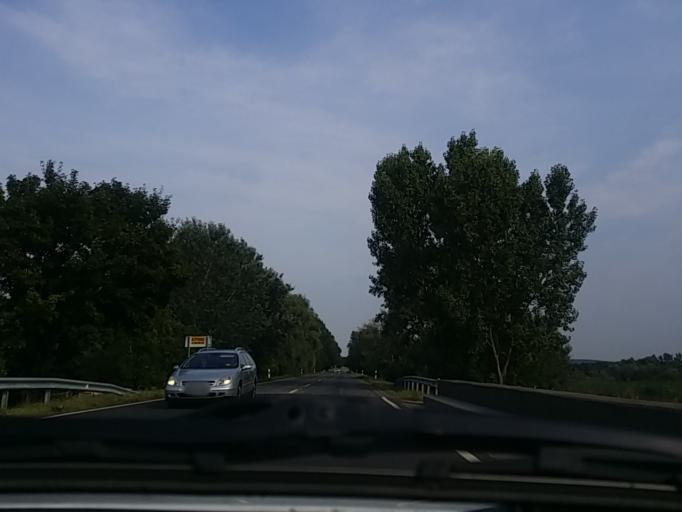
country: HU
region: Fejer
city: Bicske
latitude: 47.4966
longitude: 18.6413
